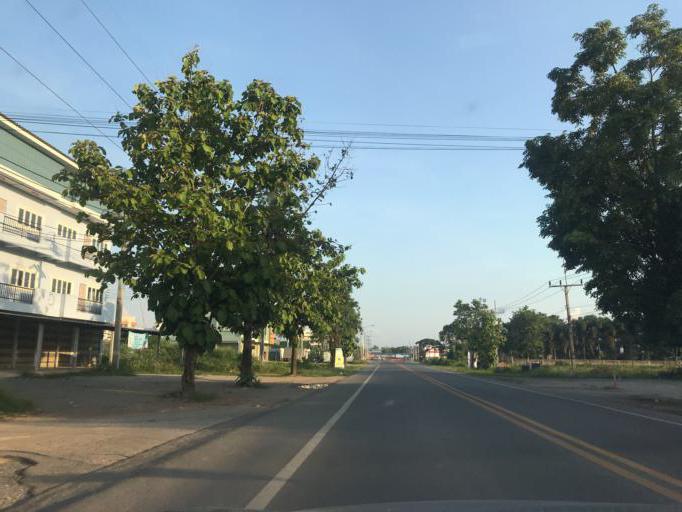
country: TH
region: Phayao
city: Chiang Kham
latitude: 19.5228
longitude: 100.2952
